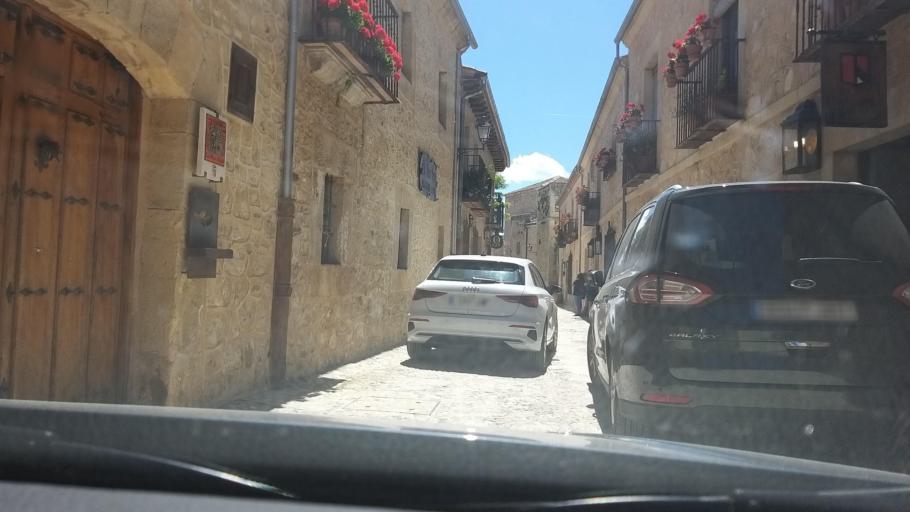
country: ES
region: Castille and Leon
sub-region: Provincia de Segovia
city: Pedraza
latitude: 41.1318
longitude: -3.8110
